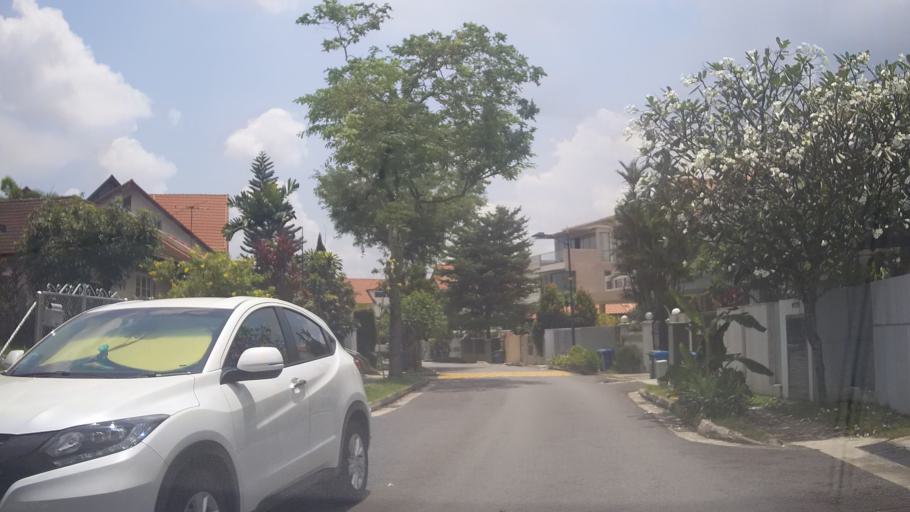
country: SG
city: Singapore
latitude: 1.3646
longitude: 103.8694
